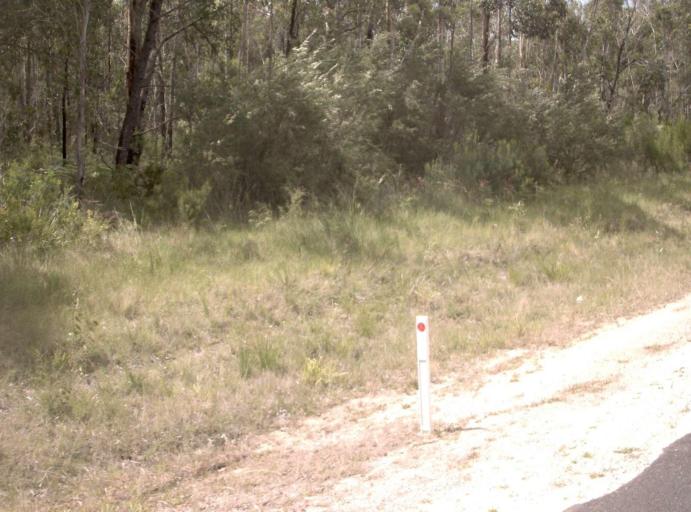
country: AU
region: New South Wales
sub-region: Bombala
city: Bombala
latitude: -37.5447
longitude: 149.4403
